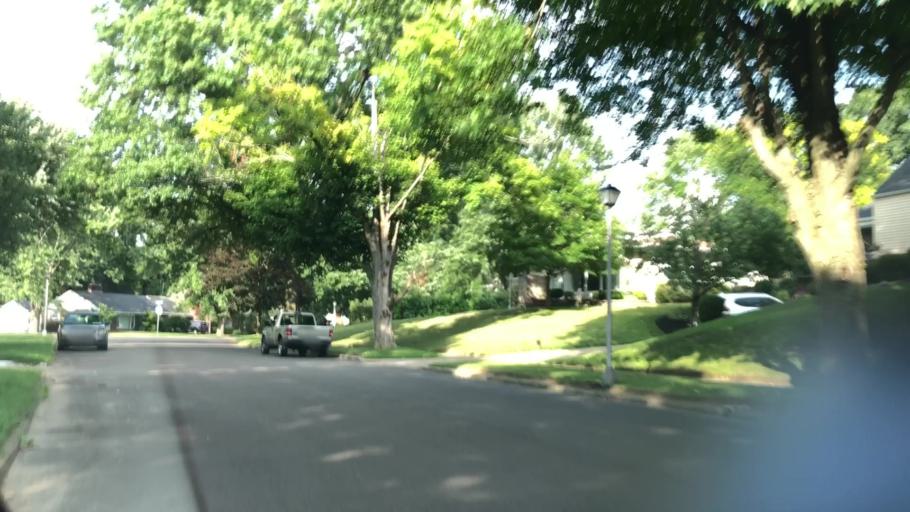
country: US
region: Ohio
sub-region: Stark County
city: Massillon
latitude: 40.8133
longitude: -81.5162
